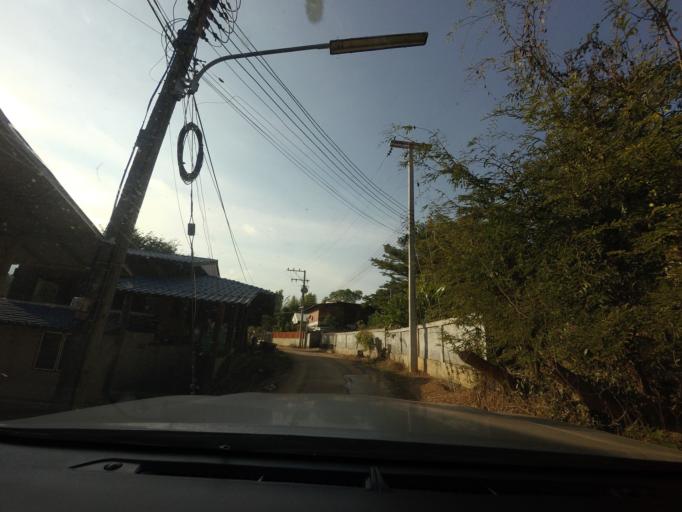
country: TH
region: Mae Hong Son
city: Wiang Nuea
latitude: 19.3986
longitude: 98.4053
